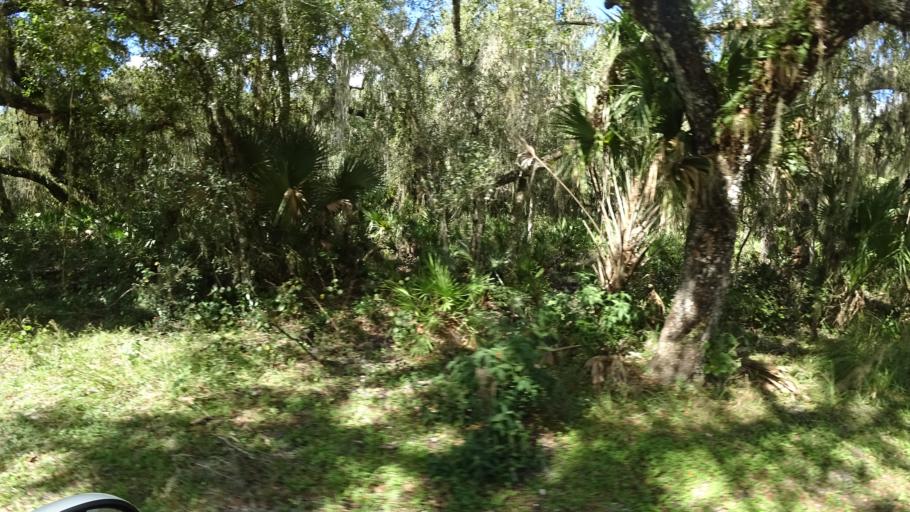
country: US
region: Florida
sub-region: Sarasota County
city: Lake Sarasota
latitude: 27.2782
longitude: -82.2649
